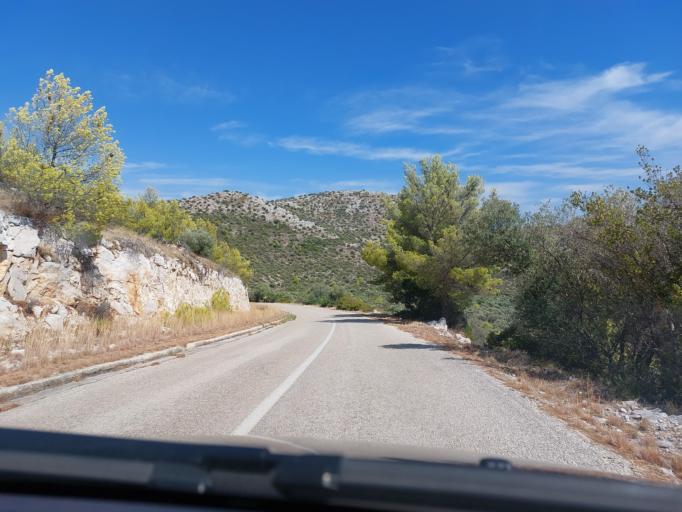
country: HR
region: Dubrovacko-Neretvanska
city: Smokvica
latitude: 42.7435
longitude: 16.8793
